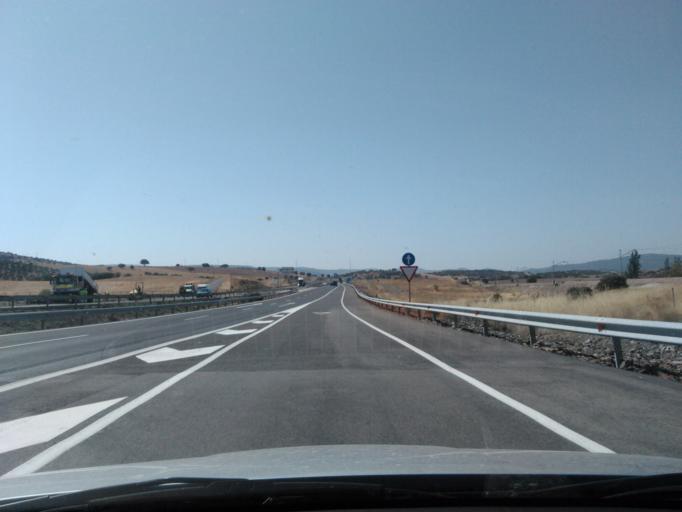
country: ES
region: Castille-La Mancha
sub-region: Provincia de Ciudad Real
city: Viso del Marques
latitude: 38.4929
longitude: -3.5029
